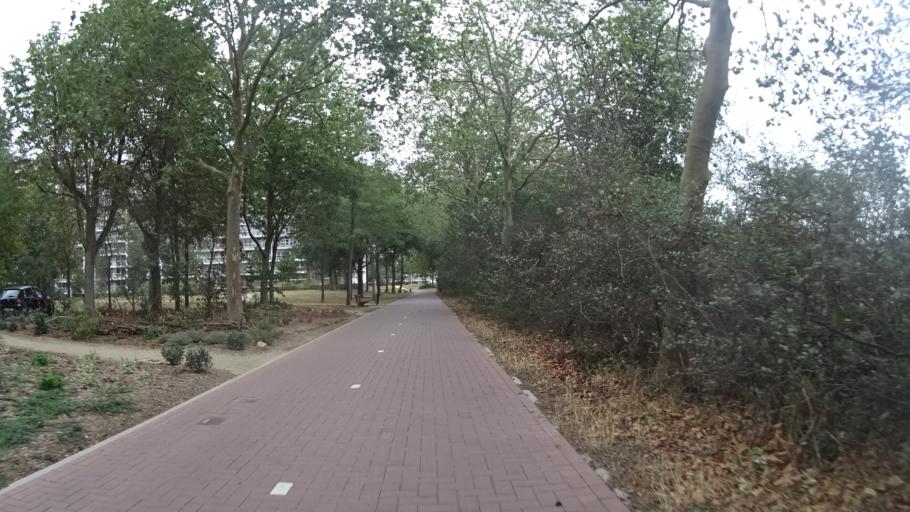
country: NL
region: Limburg
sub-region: Gemeente Venlo
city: Tegelen
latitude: 51.3593
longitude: 6.1462
